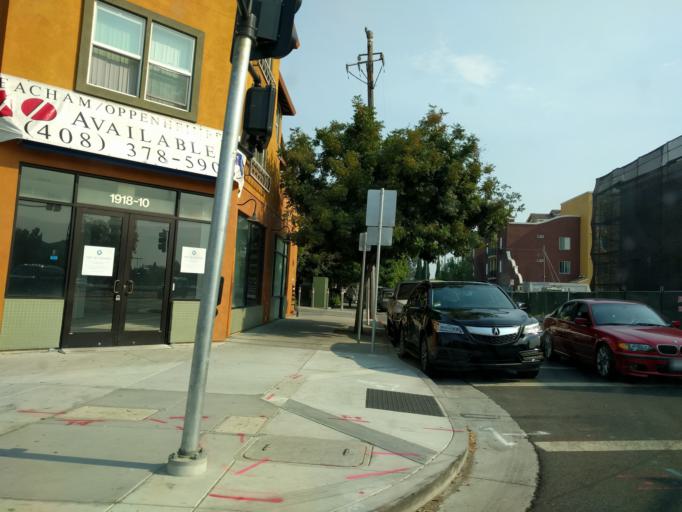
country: US
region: California
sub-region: Santa Clara County
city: Alum Rock
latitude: 37.3545
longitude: -121.8516
